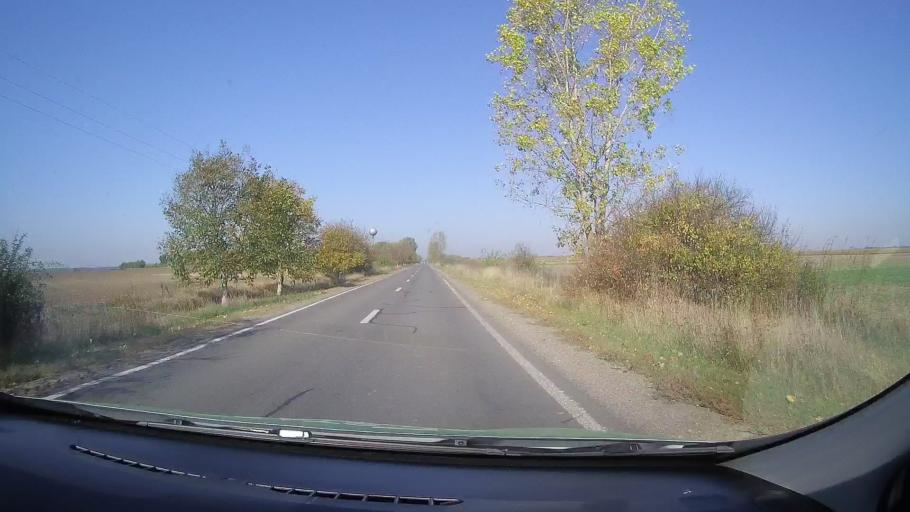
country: RO
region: Satu Mare
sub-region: Comuna Urziceni
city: Urziceni
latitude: 47.7194
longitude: 22.4177
